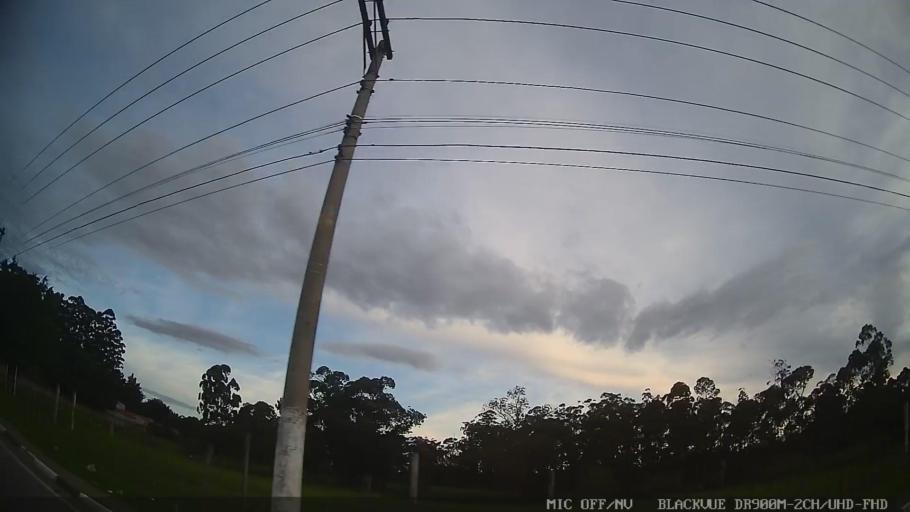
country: BR
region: Sao Paulo
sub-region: Suzano
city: Suzano
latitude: -23.5201
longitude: -46.2993
